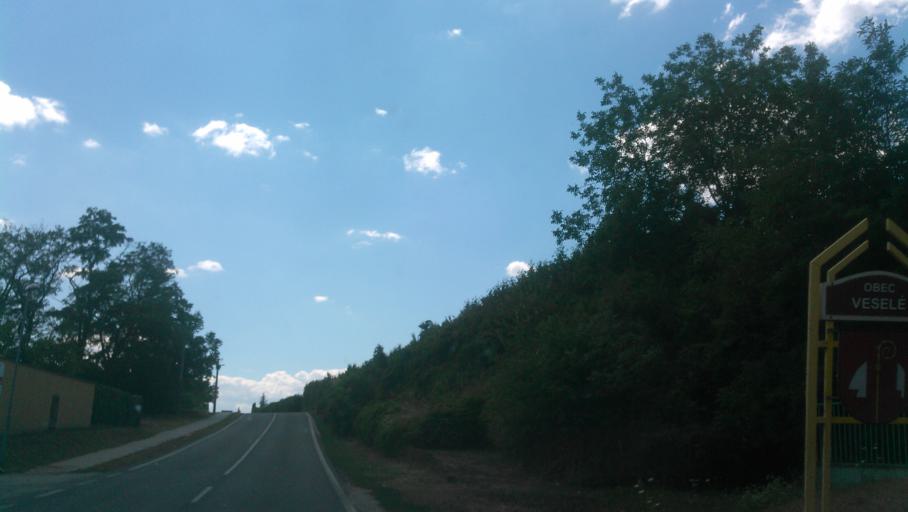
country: SK
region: Trnavsky
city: Vrbove
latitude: 48.5549
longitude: 17.7357
